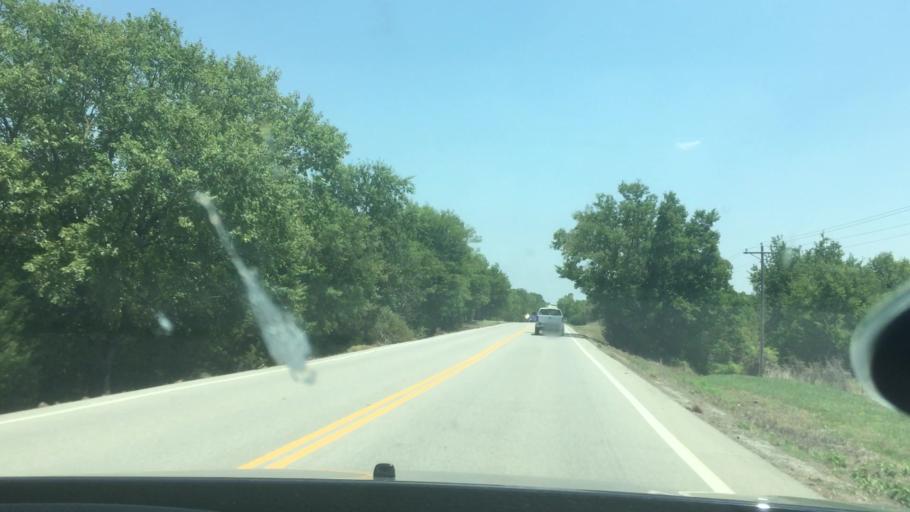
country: US
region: Oklahoma
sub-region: Bryan County
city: Durant
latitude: 34.1588
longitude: -96.3912
